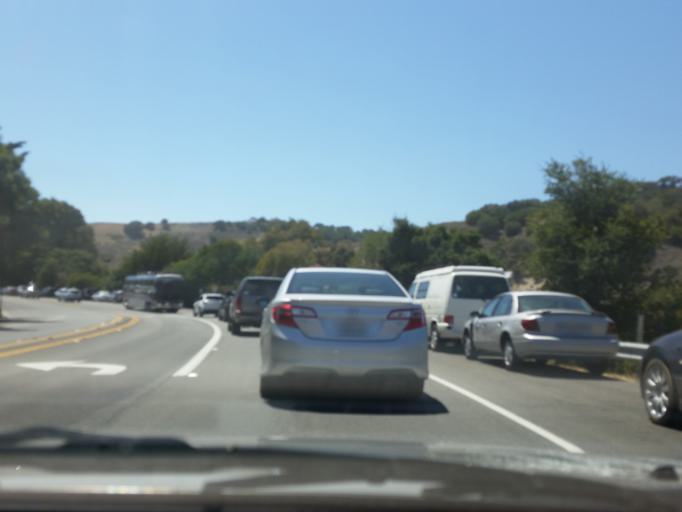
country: US
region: California
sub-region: San Luis Obispo County
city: Avila Beach
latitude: 35.1823
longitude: -120.7319
